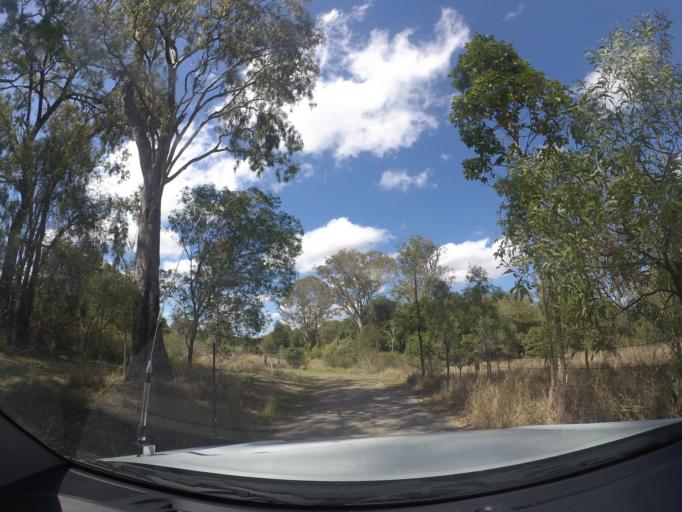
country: AU
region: Queensland
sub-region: Logan
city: Cedar Vale
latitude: -27.8437
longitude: 152.9737
